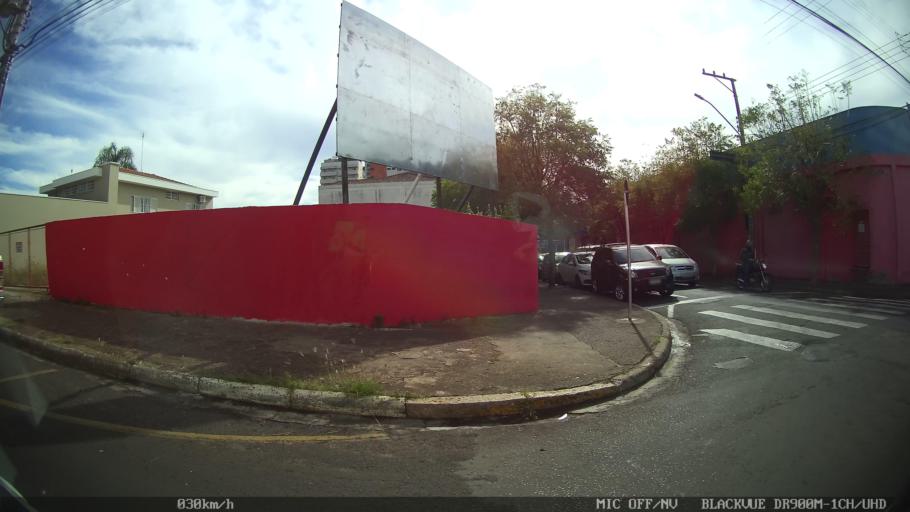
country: BR
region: Sao Paulo
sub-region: Catanduva
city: Catanduva
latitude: -21.1374
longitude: -48.9767
